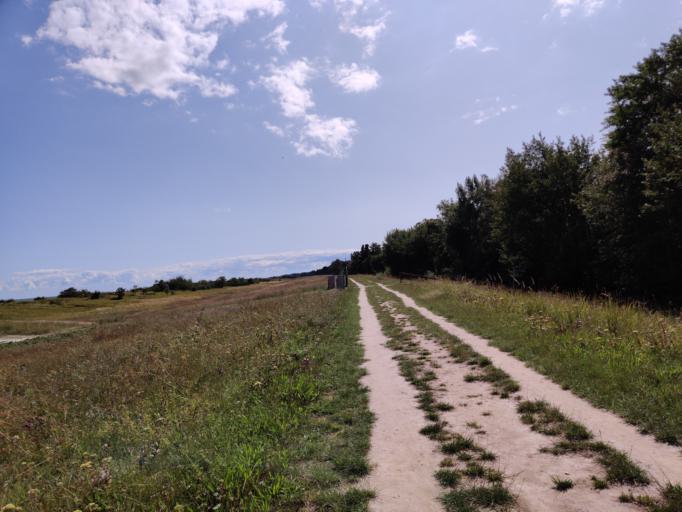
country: DK
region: Zealand
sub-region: Guldborgsund Kommune
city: Nykobing Falster
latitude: 54.6699
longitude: 11.9607
